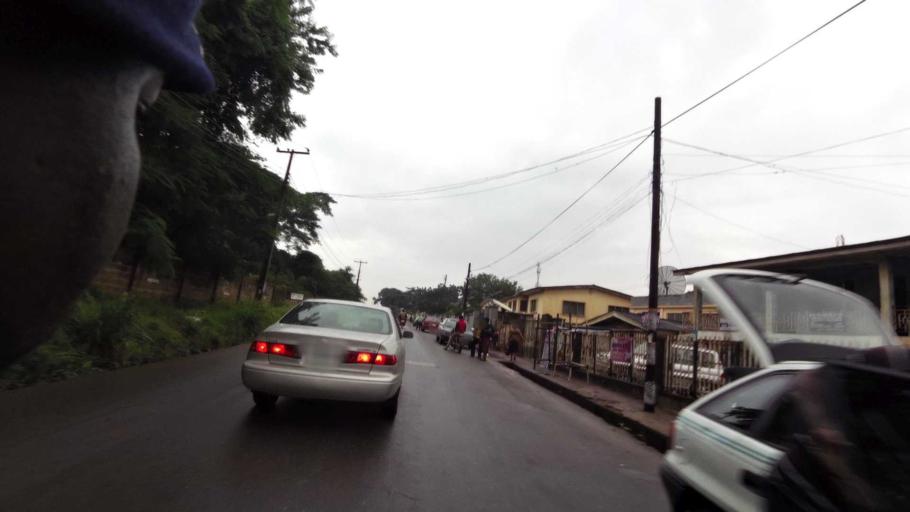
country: NG
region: Oyo
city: Ibadan
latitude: 7.4046
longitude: 3.9268
